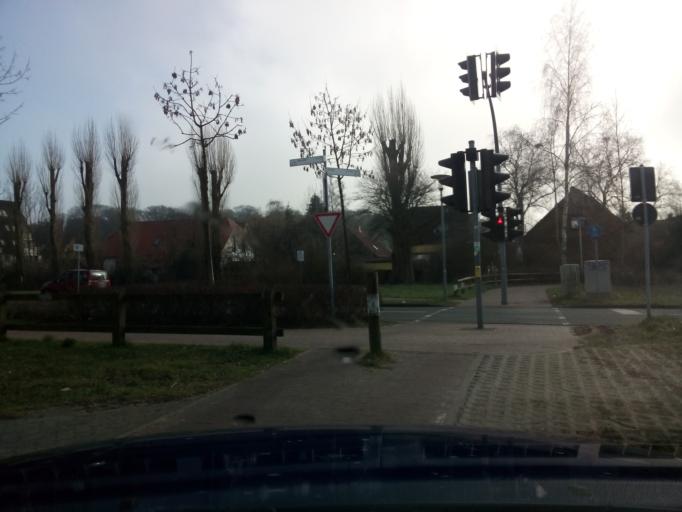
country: DE
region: Lower Saxony
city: Lilienthal
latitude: 53.1457
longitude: 8.9069
